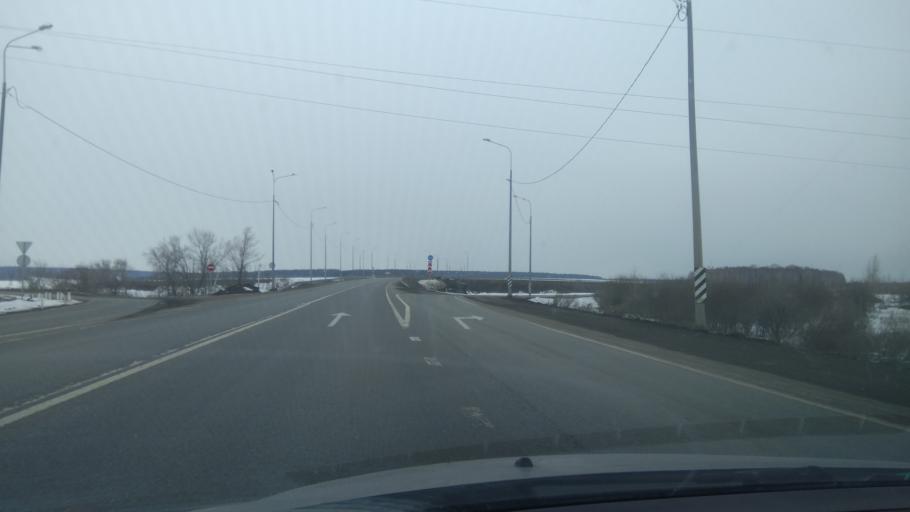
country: RU
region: Sverdlovsk
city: Achit
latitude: 56.7867
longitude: 57.8870
